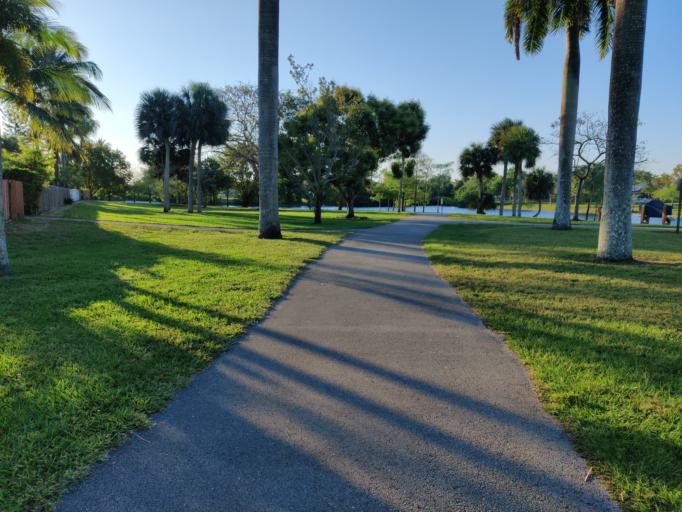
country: US
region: Florida
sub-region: Miami-Dade County
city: The Hammocks
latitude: 25.6672
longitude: -80.4544
